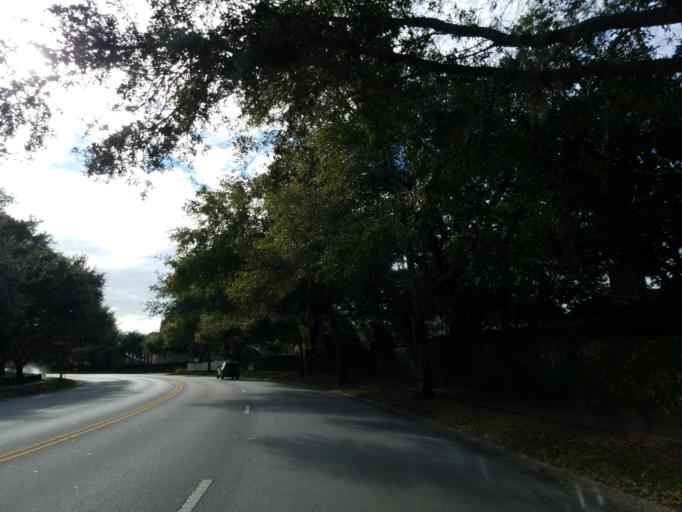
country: US
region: Florida
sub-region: Hillsborough County
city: Bloomingdale
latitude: 27.8847
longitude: -82.2643
